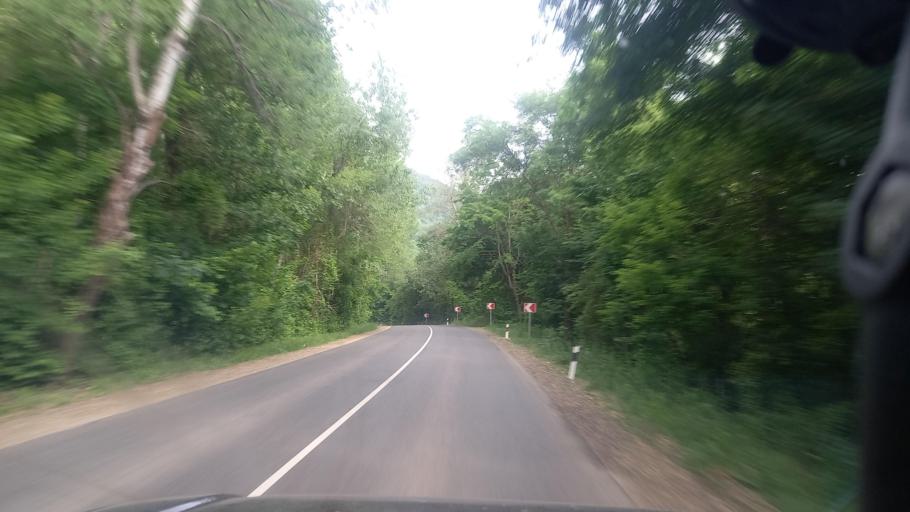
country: RU
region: Krasnodarskiy
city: Goryachiy Klyuch
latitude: 44.6008
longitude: 39.0455
